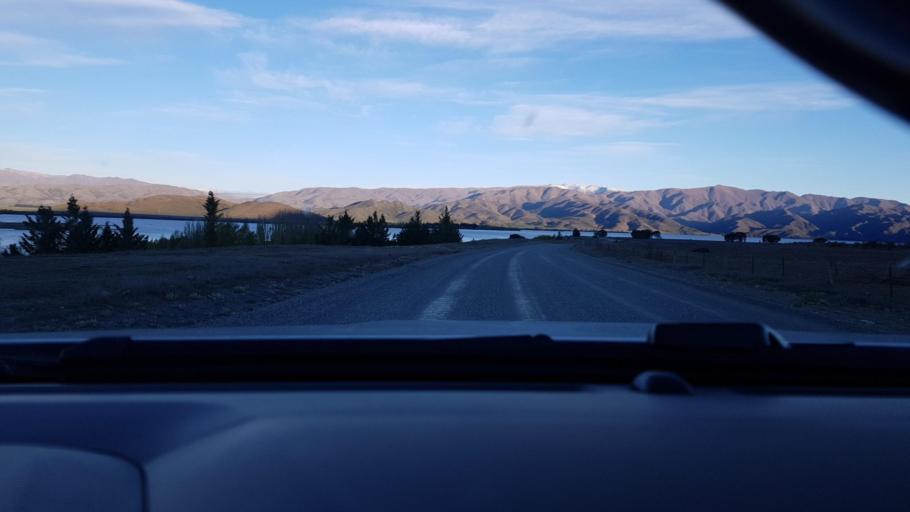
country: NZ
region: Canterbury
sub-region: Timaru District
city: Pleasant Point
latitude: -44.3469
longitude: 170.1888
